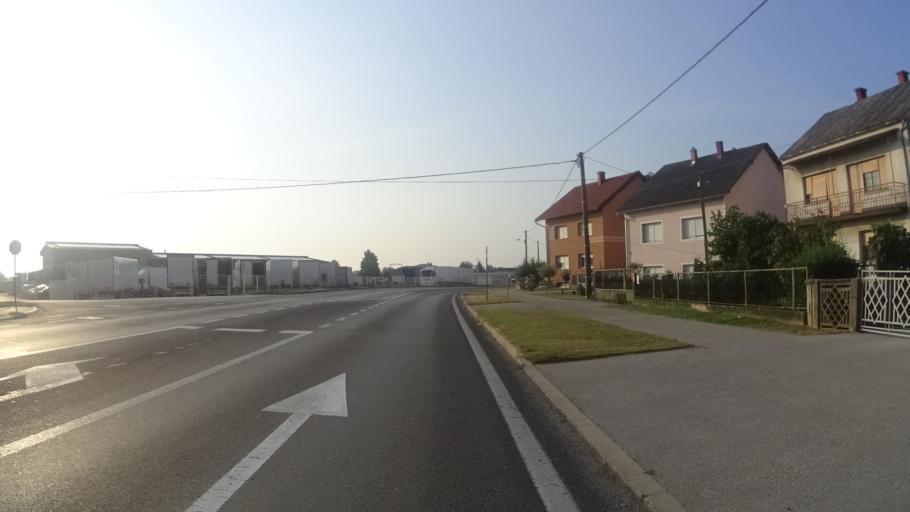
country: HR
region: Varazdinska
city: Petrijanec
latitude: 46.3394
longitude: 16.2493
